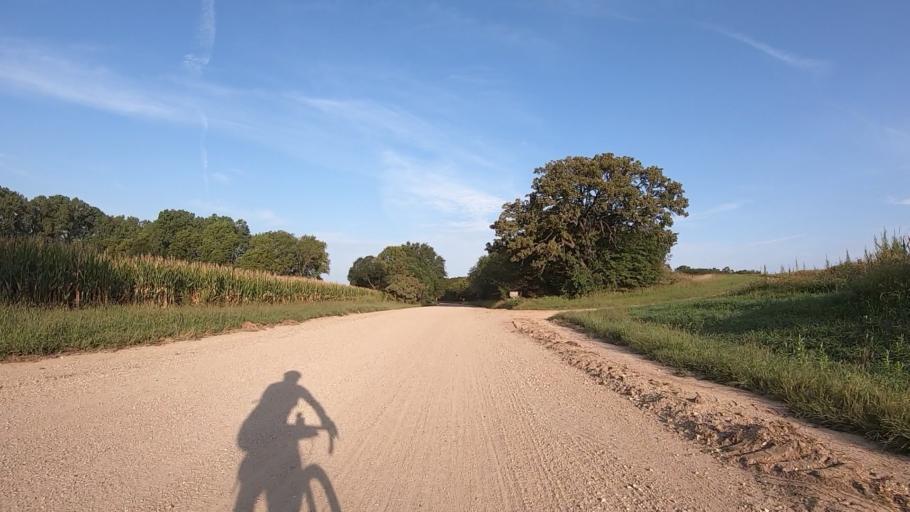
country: US
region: Kansas
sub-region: Marshall County
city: Blue Rapids
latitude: 39.7211
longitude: -96.7715
